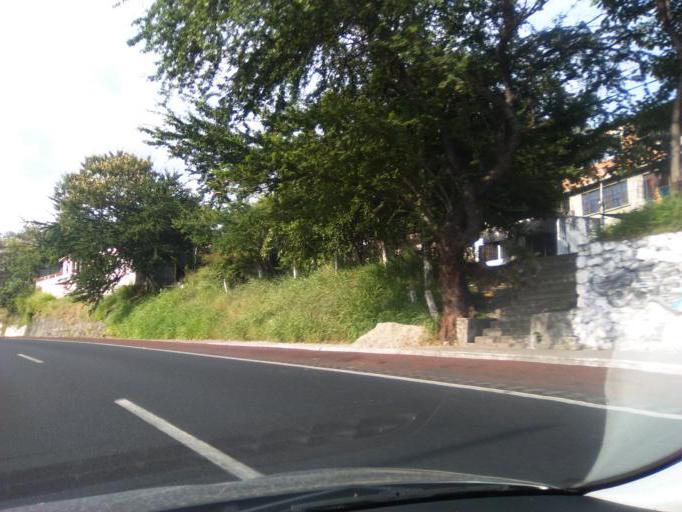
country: MX
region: Morelos
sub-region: Emiliano Zapata
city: Tres de Mayo
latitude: 18.8723
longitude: -99.2255
